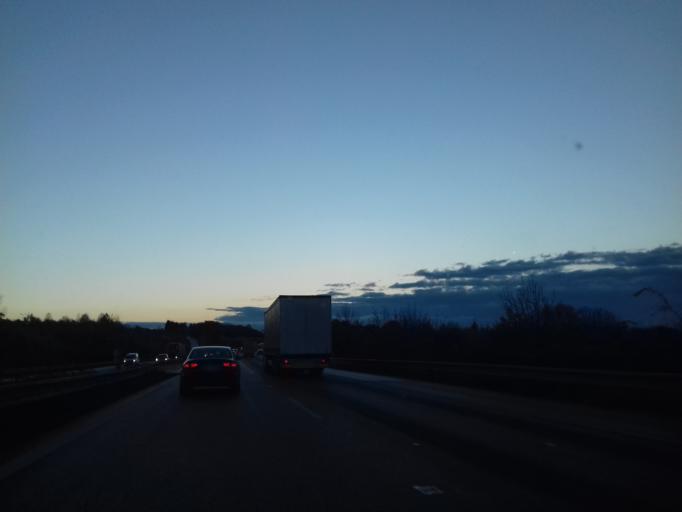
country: CZ
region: South Moravian
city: Tvarozna
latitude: 49.1863
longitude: 16.7523
